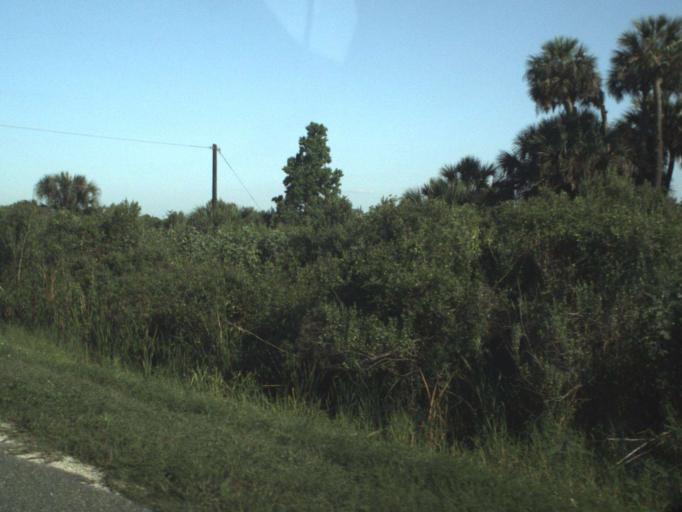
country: US
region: Florida
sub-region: Seminole County
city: Geneva
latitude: 28.7158
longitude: -81.0486
